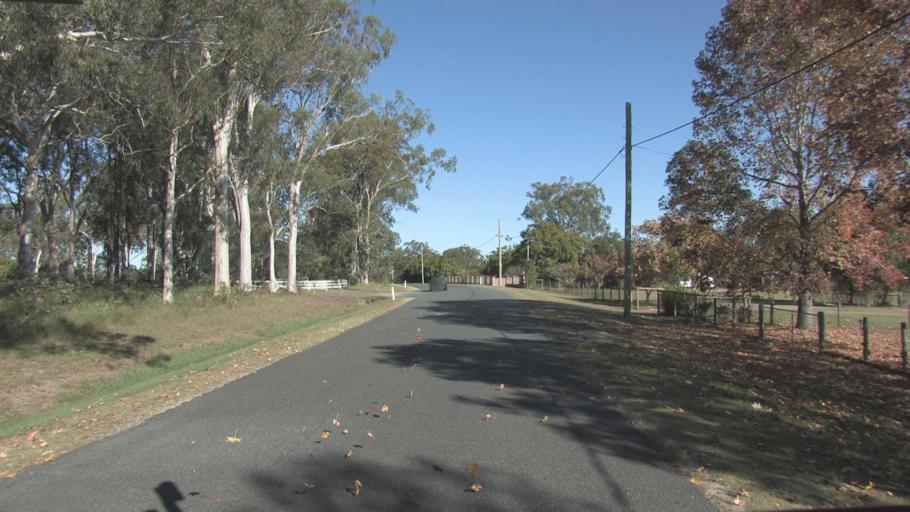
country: AU
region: Queensland
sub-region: Logan
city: Chambers Flat
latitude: -27.7372
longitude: 153.0777
